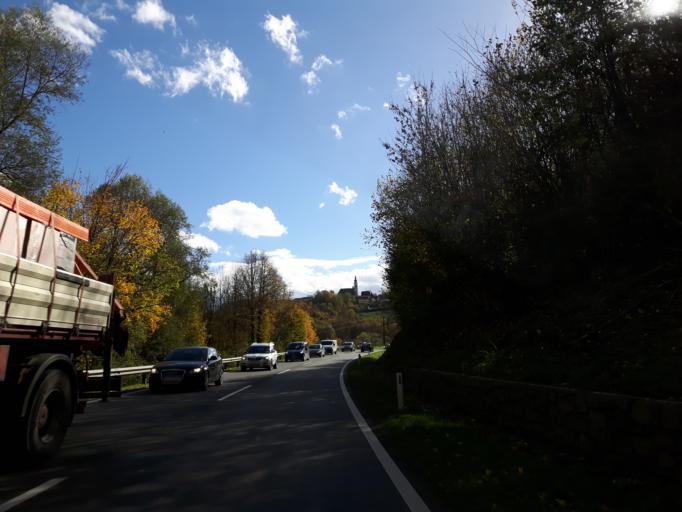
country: AT
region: Styria
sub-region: Politischer Bezirk Leibnitz
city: Seggauberg
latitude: 46.7820
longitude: 15.5178
